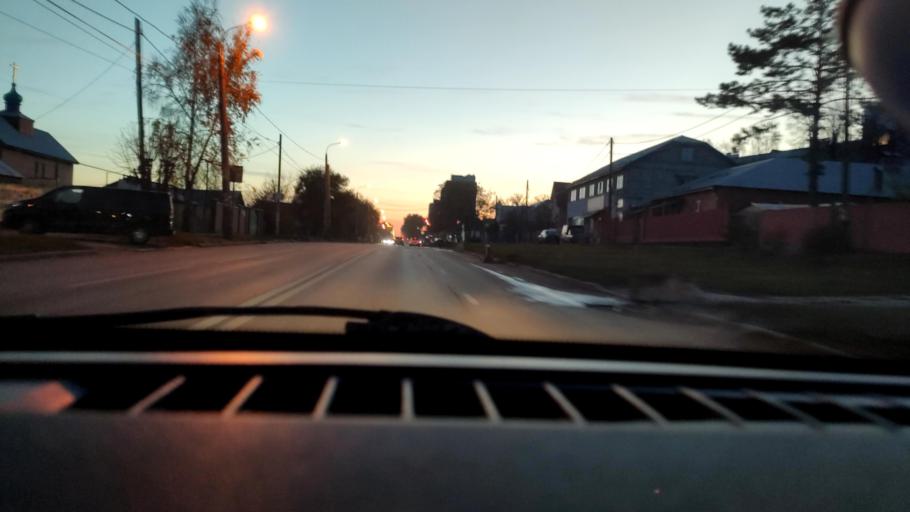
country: RU
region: Samara
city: Samara
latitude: 53.1893
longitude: 50.2090
